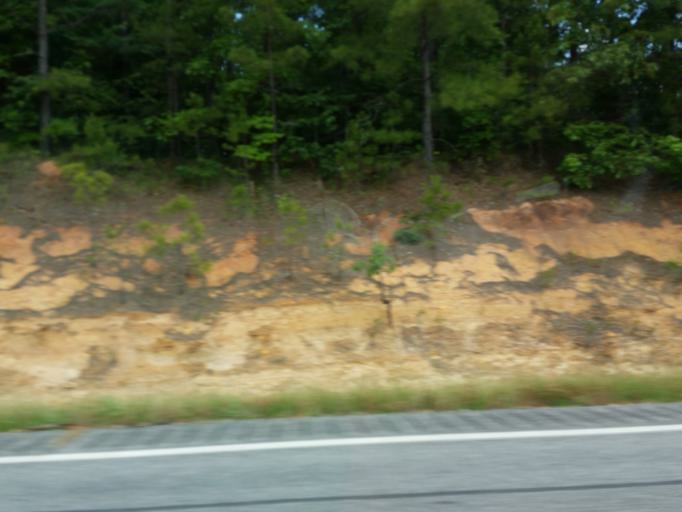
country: US
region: Alabama
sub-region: Sumter County
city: York
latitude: 32.3670
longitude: -88.1914
